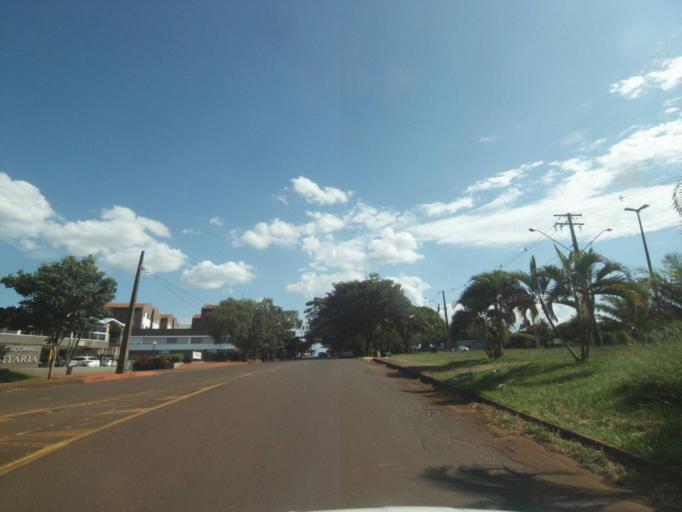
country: BR
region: Parana
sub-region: Londrina
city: Londrina
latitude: -23.3250
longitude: -51.1939
